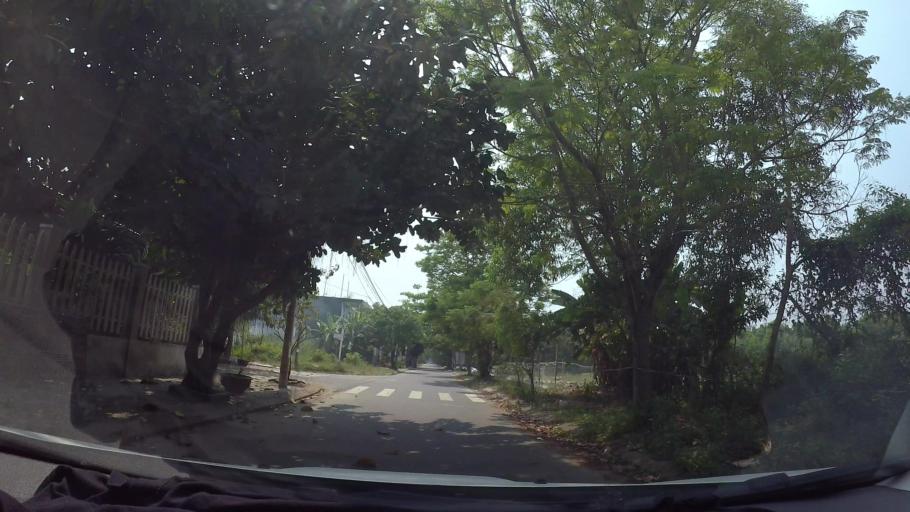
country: VN
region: Da Nang
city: Cam Le
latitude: 15.9865
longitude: 108.2067
